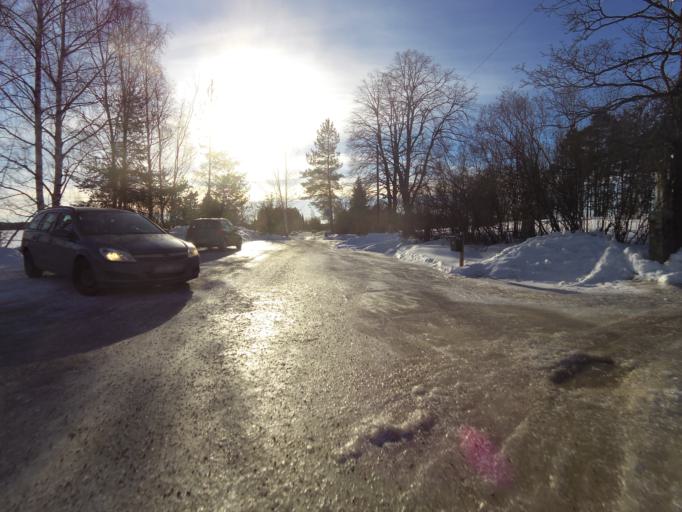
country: SE
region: Gaevleborg
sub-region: Gavle Kommun
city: Valbo
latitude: 60.6230
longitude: 16.9799
